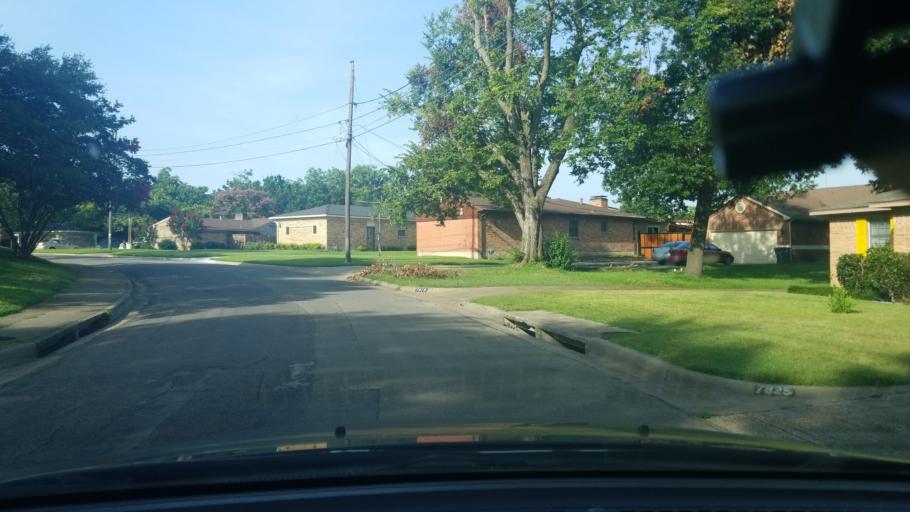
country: US
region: Texas
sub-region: Dallas County
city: Highland Park
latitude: 32.7966
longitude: -96.7130
